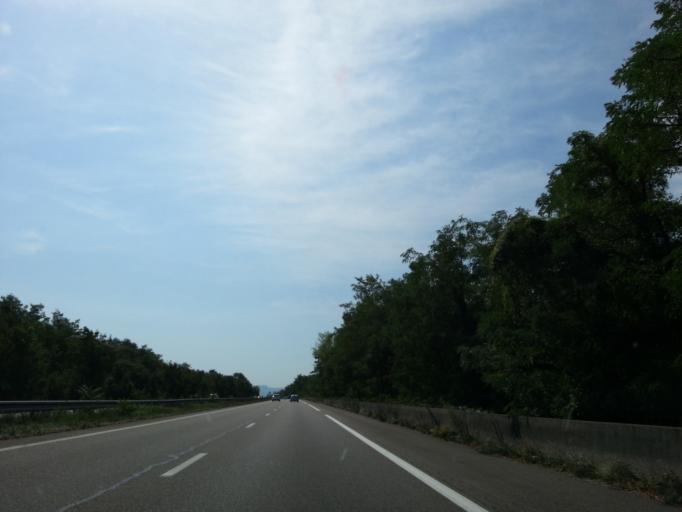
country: FR
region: Alsace
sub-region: Departement du Haut-Rhin
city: Blotzheim
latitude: 47.6238
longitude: 7.5092
